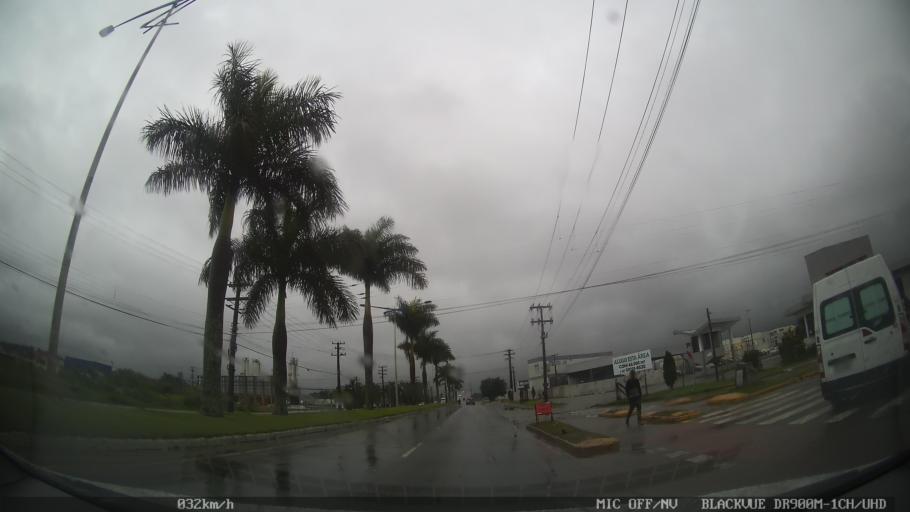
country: BR
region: Santa Catarina
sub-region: Itajai
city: Itajai
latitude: -26.9172
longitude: -48.7057
